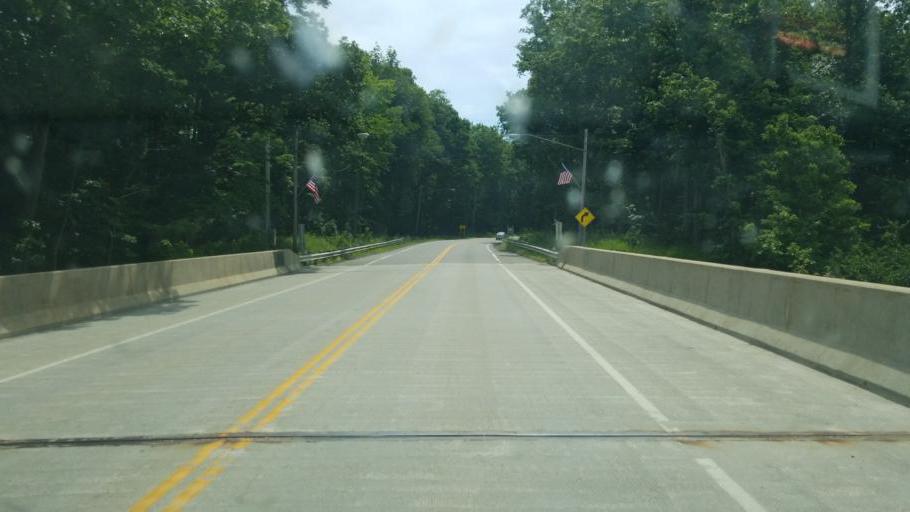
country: US
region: Ohio
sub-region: Cuyahoga County
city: Brecksville
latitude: 41.3210
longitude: -81.5850
